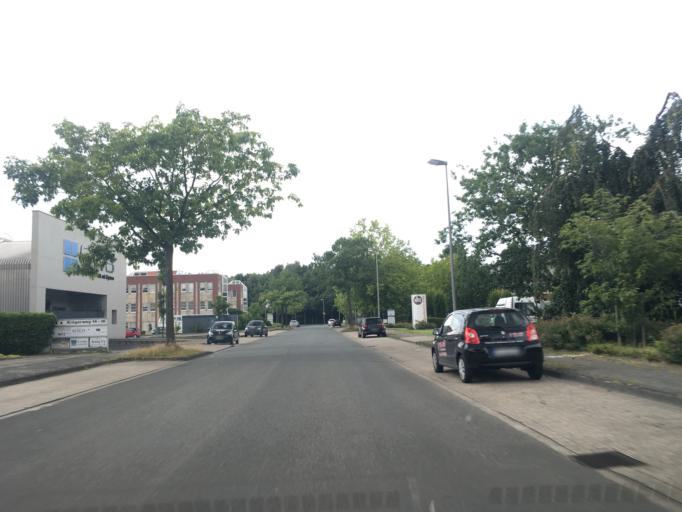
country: DE
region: North Rhine-Westphalia
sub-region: Regierungsbezirk Munster
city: Muenster
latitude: 51.9234
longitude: 7.6587
